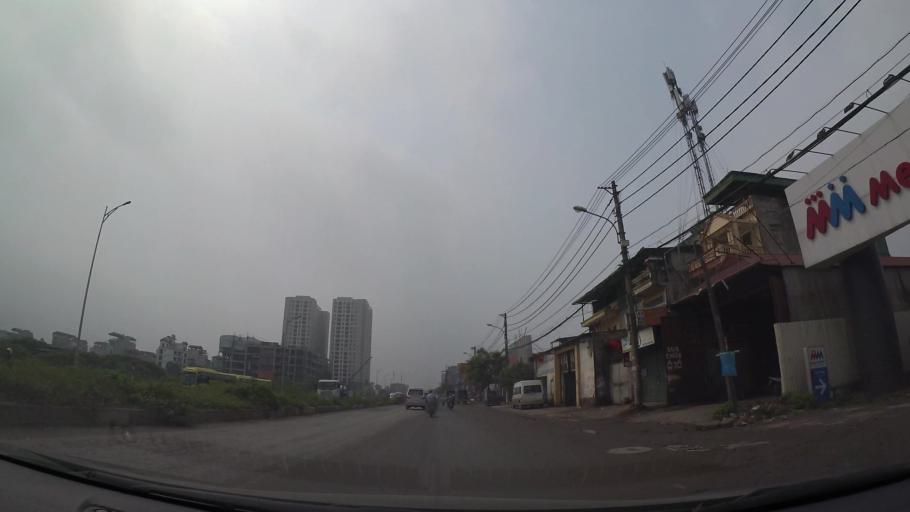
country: VN
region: Ha Noi
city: Van Dien
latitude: 20.9702
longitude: 105.8670
